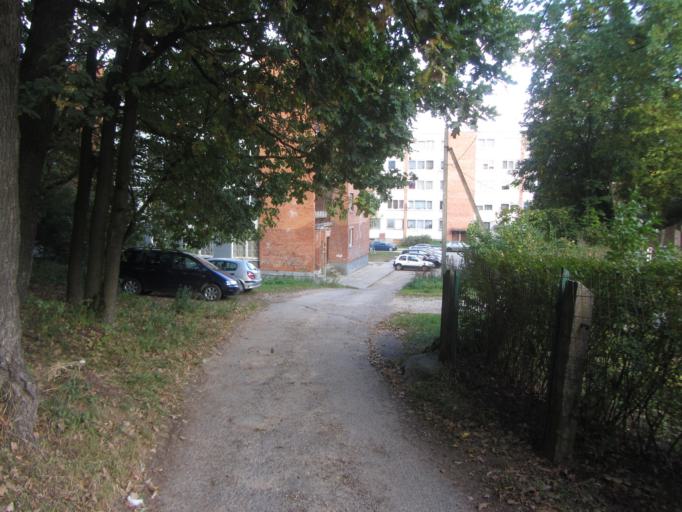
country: LT
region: Vilnius County
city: Lazdynai
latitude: 54.6421
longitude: 25.2024
